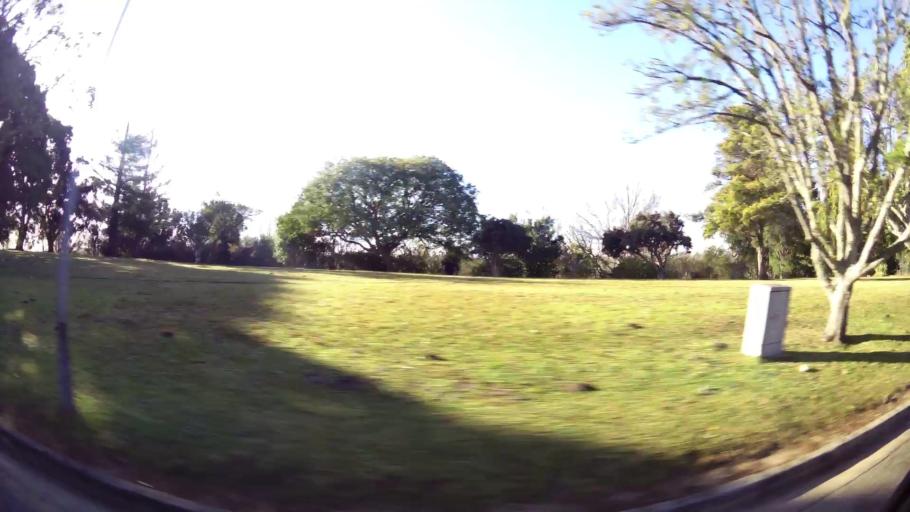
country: ZA
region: Western Cape
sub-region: Eden District Municipality
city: George
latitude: -33.9514
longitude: 22.4543
